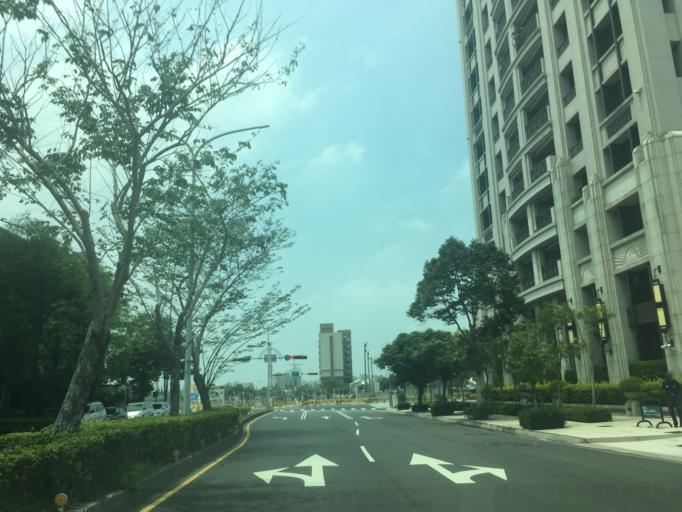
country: TW
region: Taiwan
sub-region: Taichung City
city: Taichung
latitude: 24.1856
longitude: 120.6832
